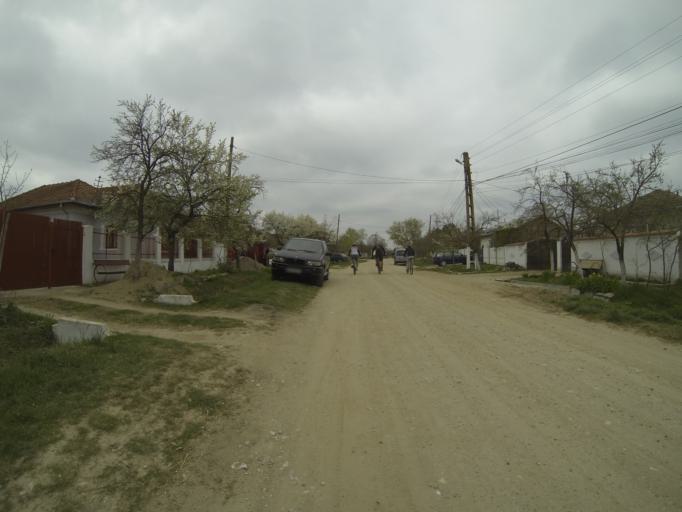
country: RO
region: Dolj
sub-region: Comuna Breasta
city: Breasta
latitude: 44.3398
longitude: 23.6799
